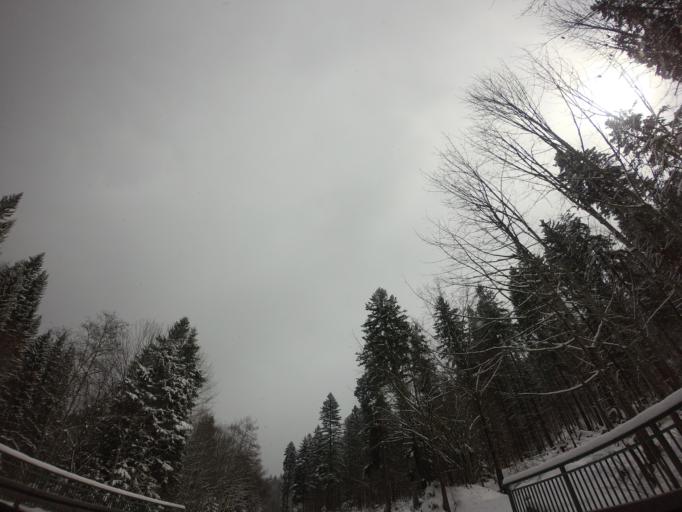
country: DE
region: Bavaria
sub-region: Upper Bavaria
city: Grainau
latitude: 47.4816
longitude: 11.0121
